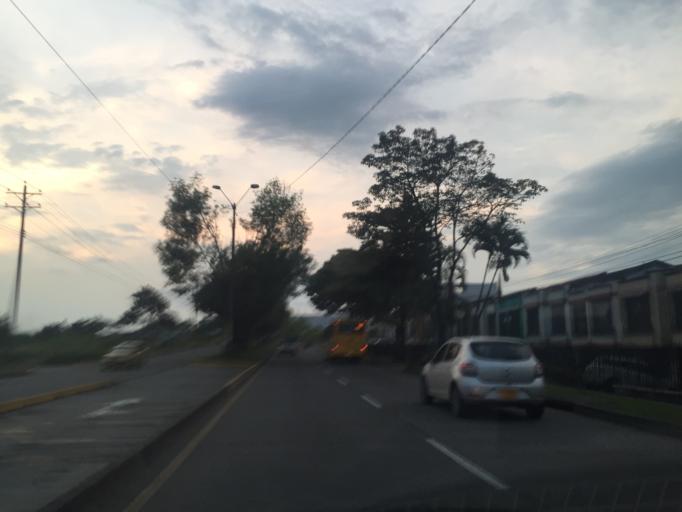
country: CO
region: Risaralda
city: Pereira
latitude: 4.7996
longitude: -75.7446
